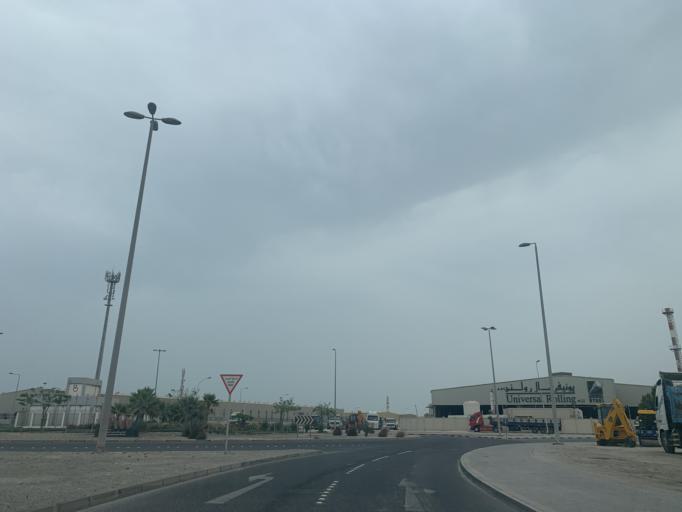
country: BH
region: Muharraq
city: Al Hadd
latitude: 26.2122
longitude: 50.6665
